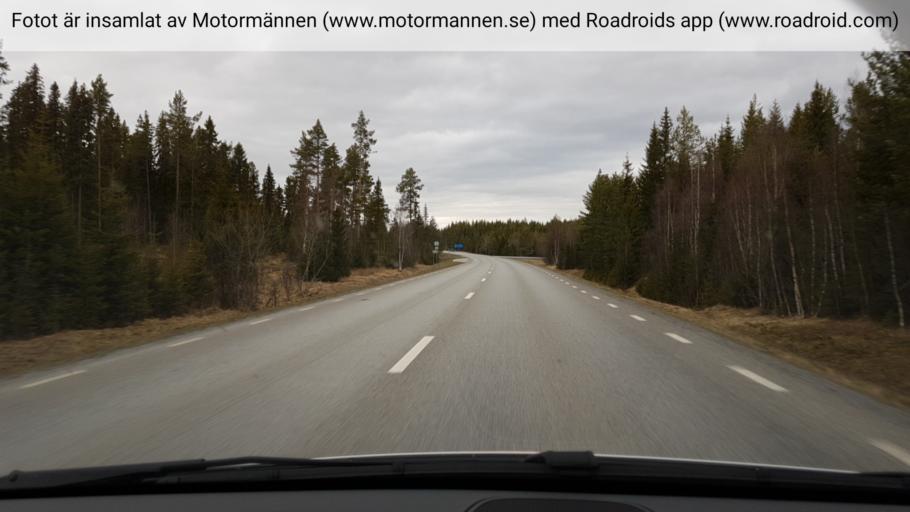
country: SE
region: Jaemtland
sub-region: Krokoms Kommun
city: Valla
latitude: 63.3024
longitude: 13.9256
